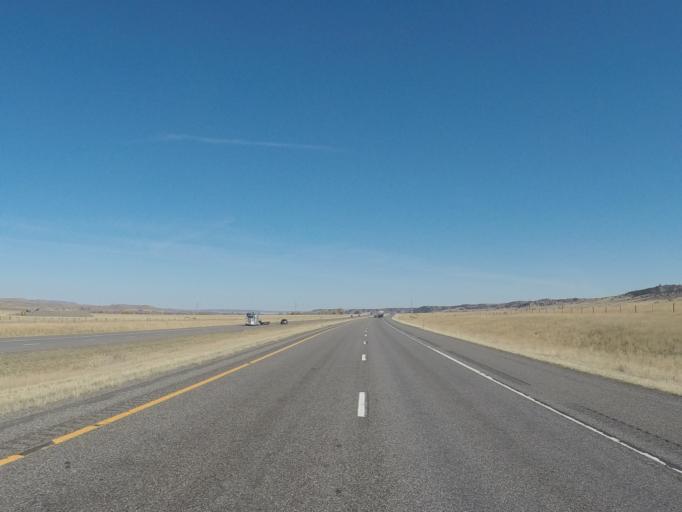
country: US
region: Montana
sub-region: Sweet Grass County
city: Big Timber
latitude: 45.7468
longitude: -110.1769
